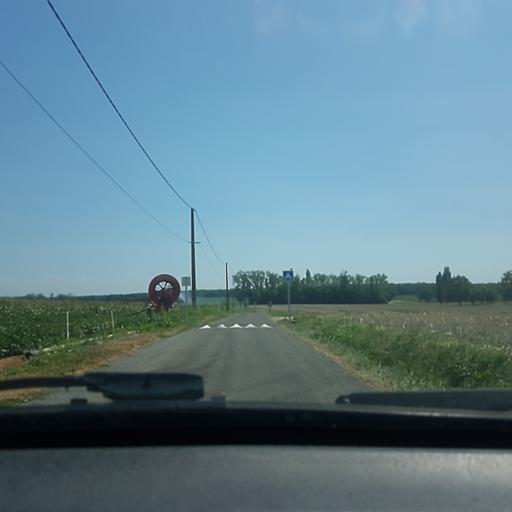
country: FR
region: Bourgogne
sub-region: Departement de Saone-et-Loire
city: Givry
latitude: 46.7802
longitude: 4.7541
